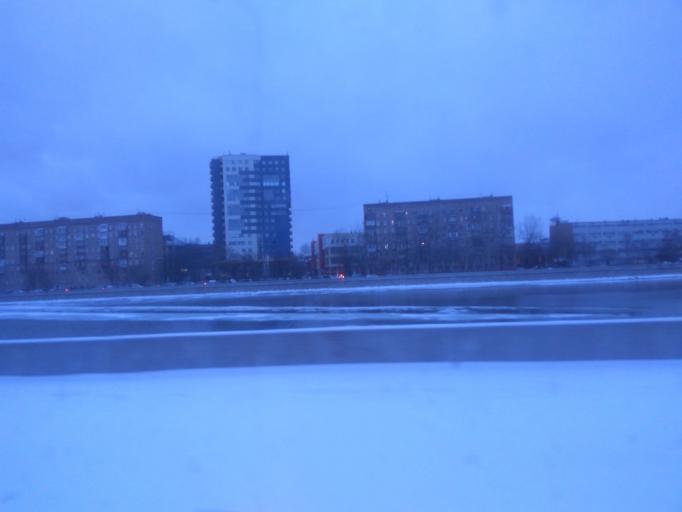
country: RU
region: Moscow
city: Taganskiy
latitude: 55.7198
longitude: 37.6559
